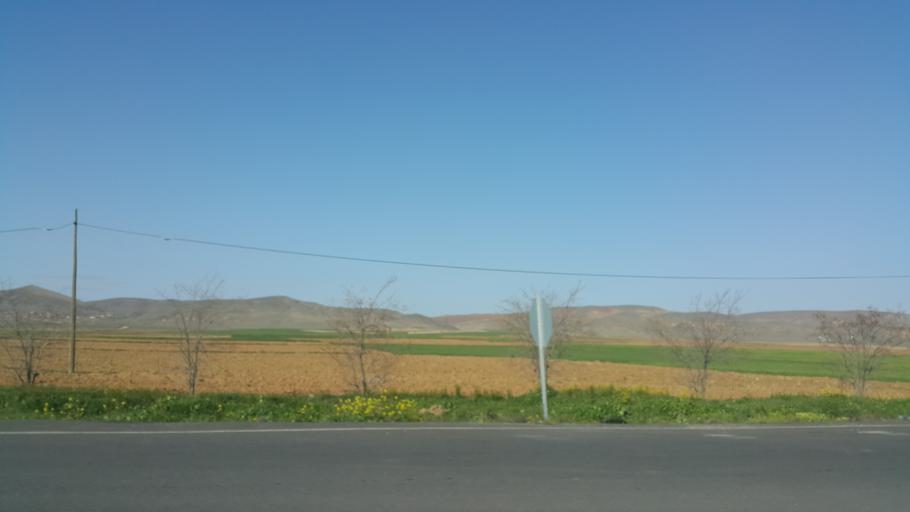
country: TR
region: Aksaray
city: Acipinar
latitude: 38.6722
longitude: 33.7071
